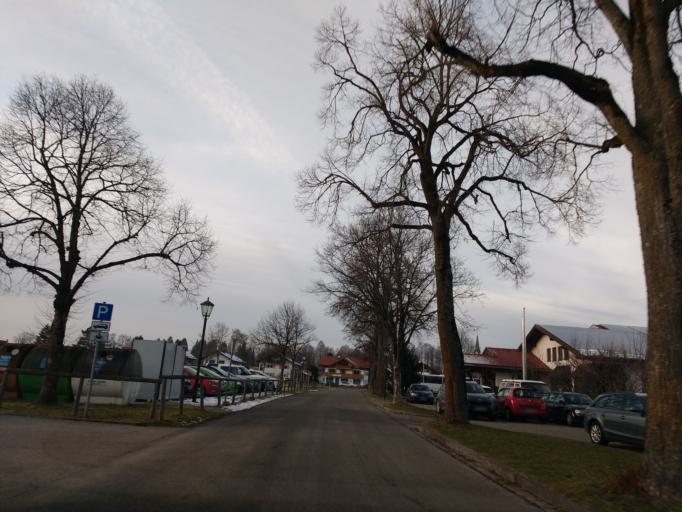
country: DE
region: Bavaria
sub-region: Swabia
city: Schwangau
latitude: 47.5737
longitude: 10.7355
